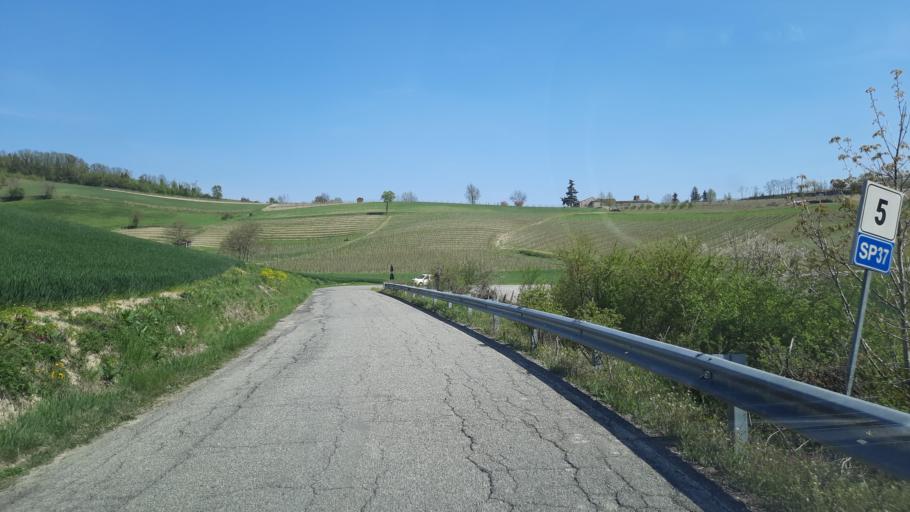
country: IT
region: Piedmont
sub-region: Provincia di Alessandria
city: Sala Monferrato
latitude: 45.0809
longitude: 8.3652
